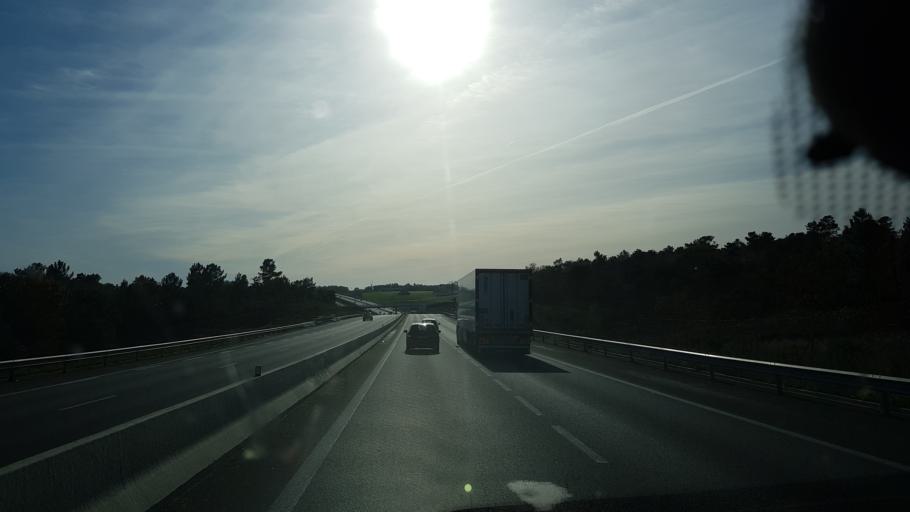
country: FR
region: Poitou-Charentes
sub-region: Departement de la Charente
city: Baignes-Sainte-Radegonde
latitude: 45.3618
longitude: -0.1902
